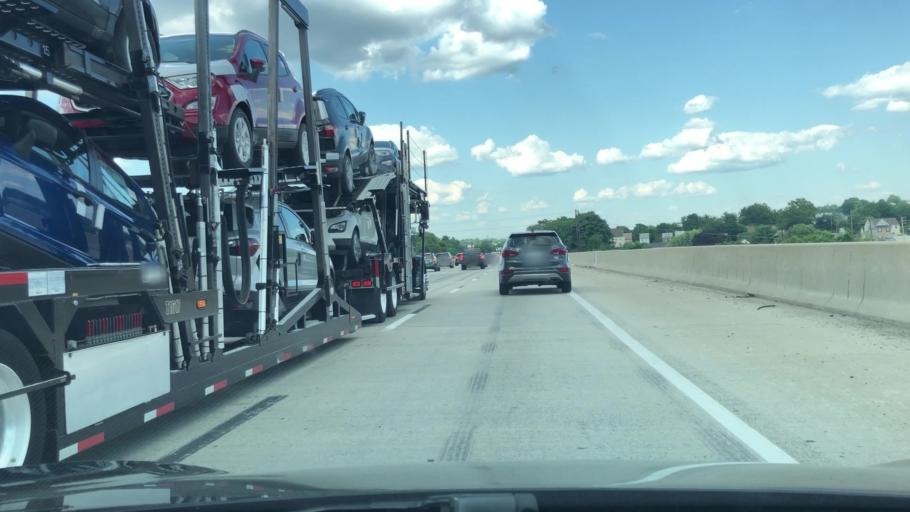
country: US
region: Pennsylvania
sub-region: Montgomery County
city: West Conshohocken
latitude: 40.0768
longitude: -75.3187
